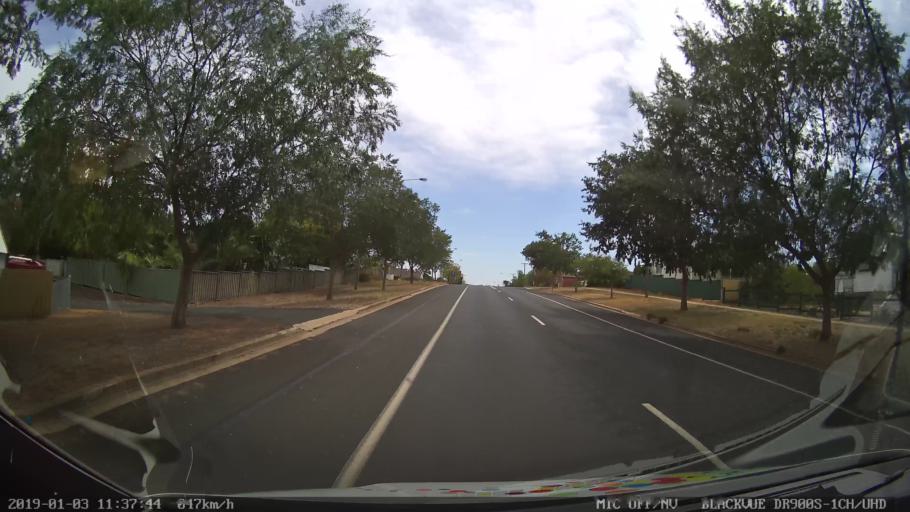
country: AU
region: New South Wales
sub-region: Weddin
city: Grenfell
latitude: -33.9010
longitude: 148.1616
